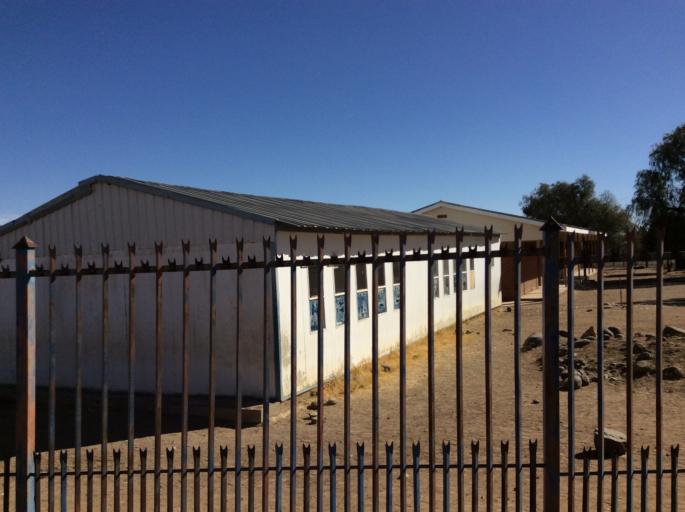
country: ZA
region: Orange Free State
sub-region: Lejweleputswa District Municipality
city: Brandfort
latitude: -28.7343
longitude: 26.1111
